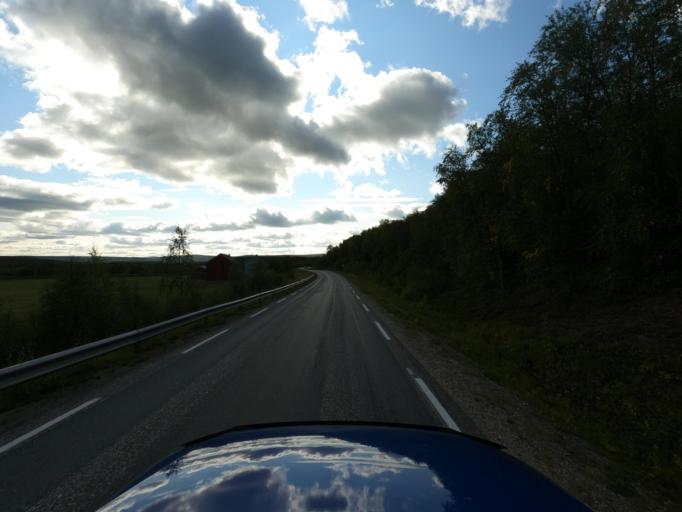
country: NO
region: Finnmark Fylke
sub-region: Karasjok
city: Karasjohka
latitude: 69.4257
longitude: 25.7938
